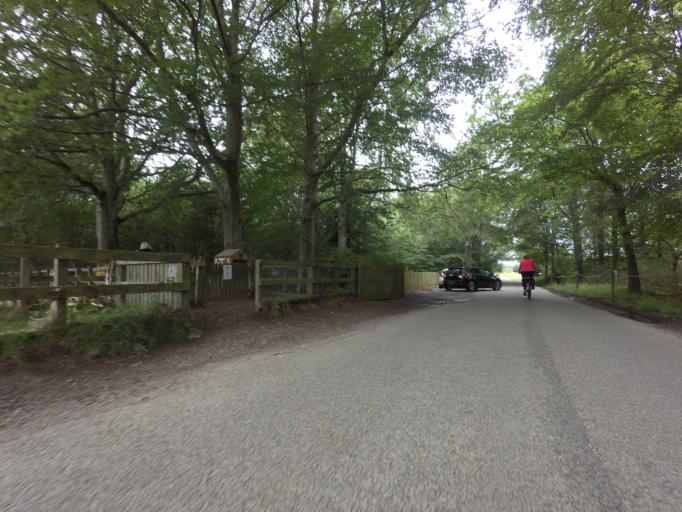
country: GB
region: Scotland
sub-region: Moray
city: Forres
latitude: 57.5959
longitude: -3.7149
